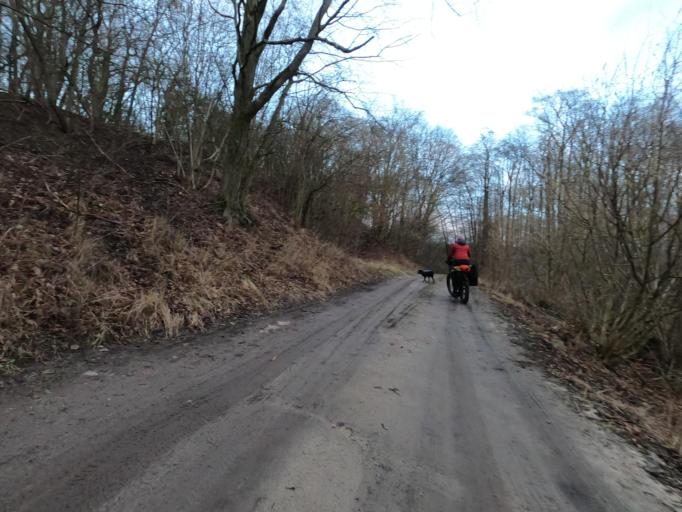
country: PL
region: Greater Poland Voivodeship
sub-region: Powiat pilski
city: Wyrzysk
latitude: 53.1167
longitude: 17.2067
